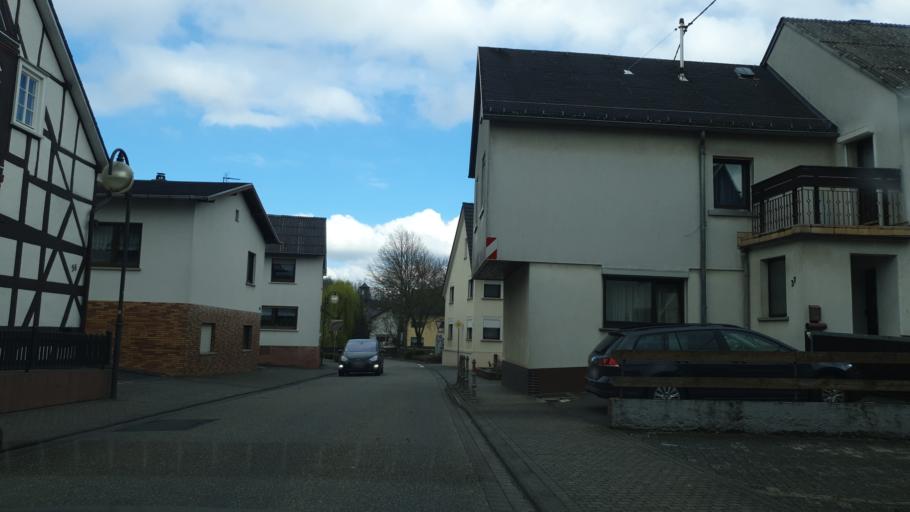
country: DE
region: Rheinland-Pfalz
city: Niederelbert
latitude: 50.4072
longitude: 7.8125
